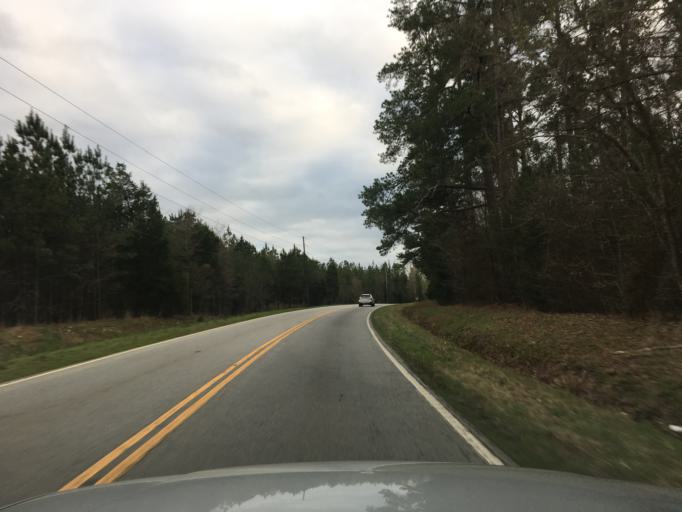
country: US
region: South Carolina
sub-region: Saluda County
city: Saluda
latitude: 33.9842
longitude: -81.7694
